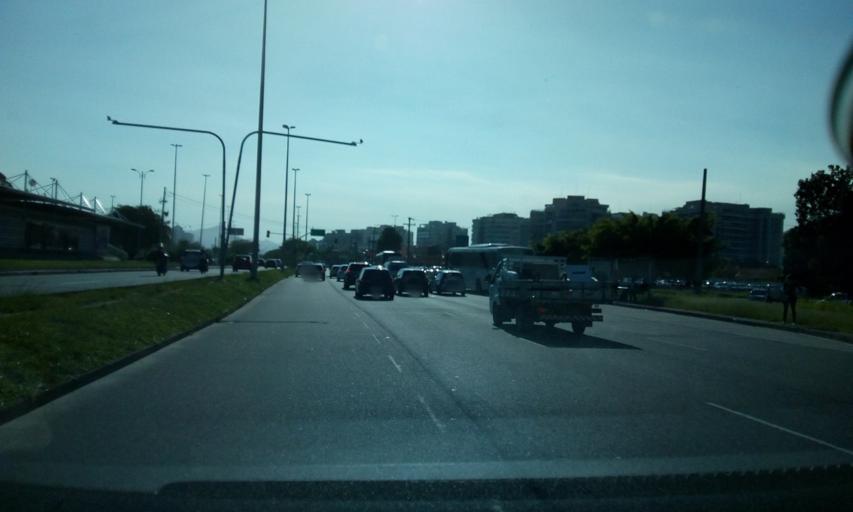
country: BR
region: Rio de Janeiro
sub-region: Nilopolis
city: Nilopolis
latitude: -23.0003
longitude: -43.4168
